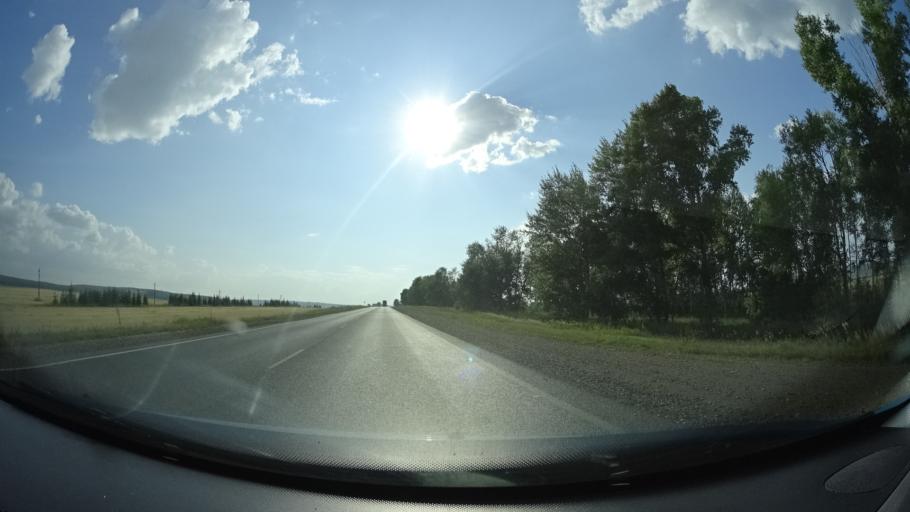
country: RU
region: Tatarstan
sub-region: Bavlinskiy Rayon
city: Bavly
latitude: 54.4772
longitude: 53.3385
